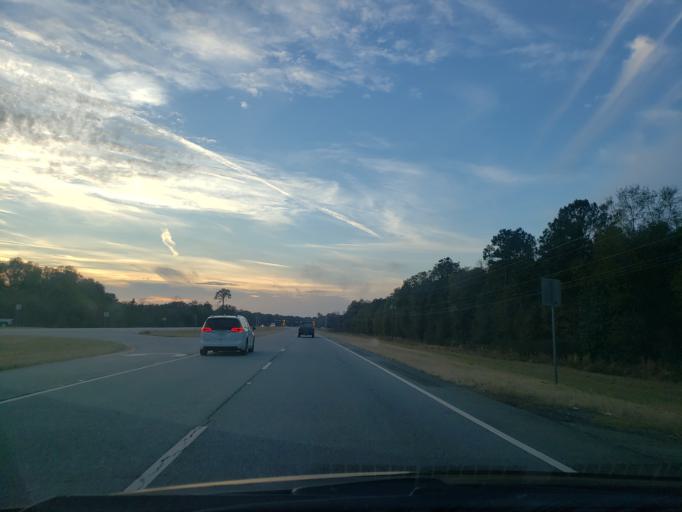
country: US
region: Georgia
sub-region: Dougherty County
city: Putney
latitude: 31.5550
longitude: -83.9912
